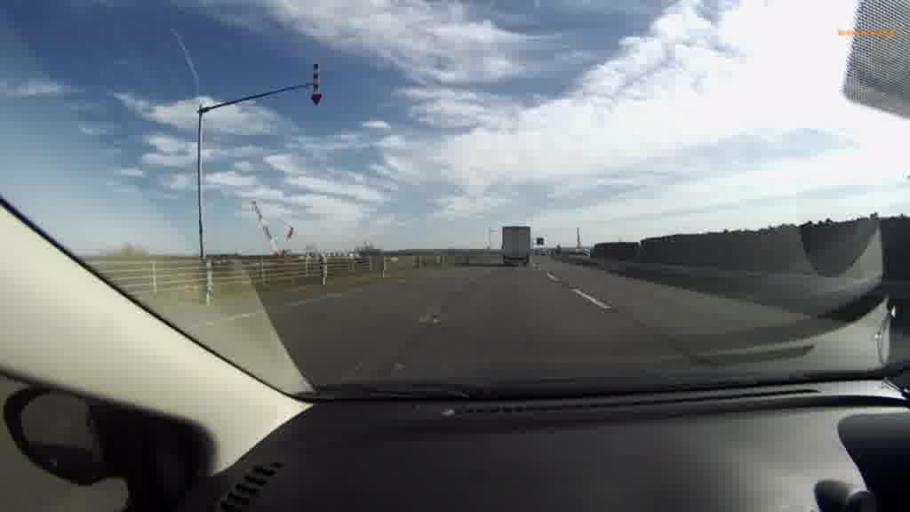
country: JP
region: Hokkaido
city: Kushiro
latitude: 43.0360
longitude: 144.3184
